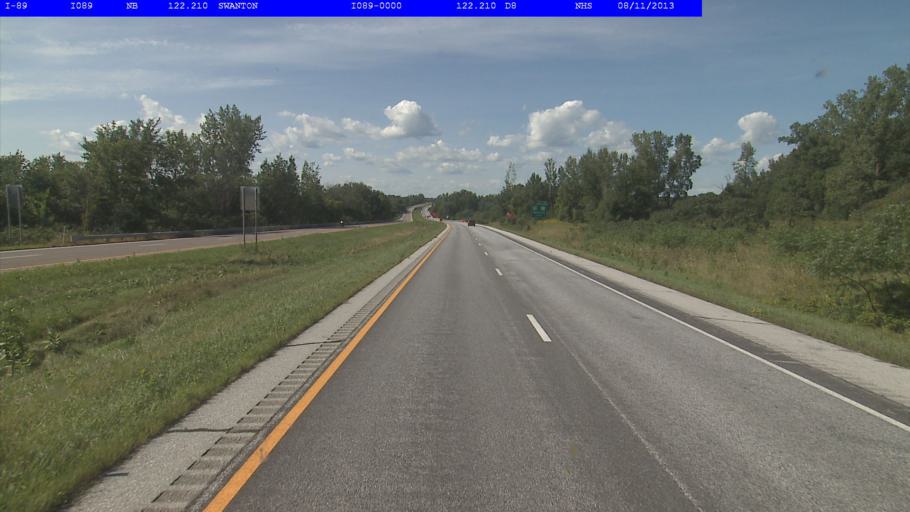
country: US
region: Vermont
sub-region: Franklin County
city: Swanton
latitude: 44.9068
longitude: -73.0982
